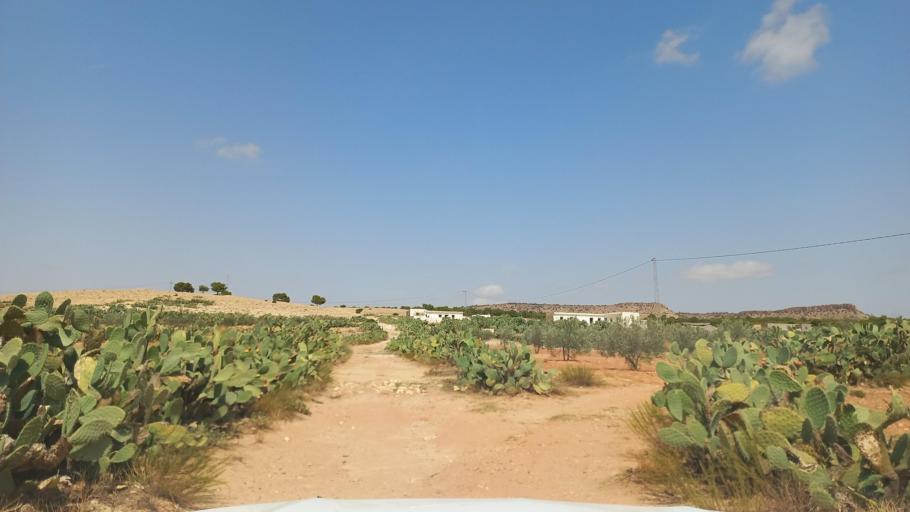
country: TN
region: Al Qasrayn
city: Sbiba
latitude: 35.4017
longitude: 8.9694
